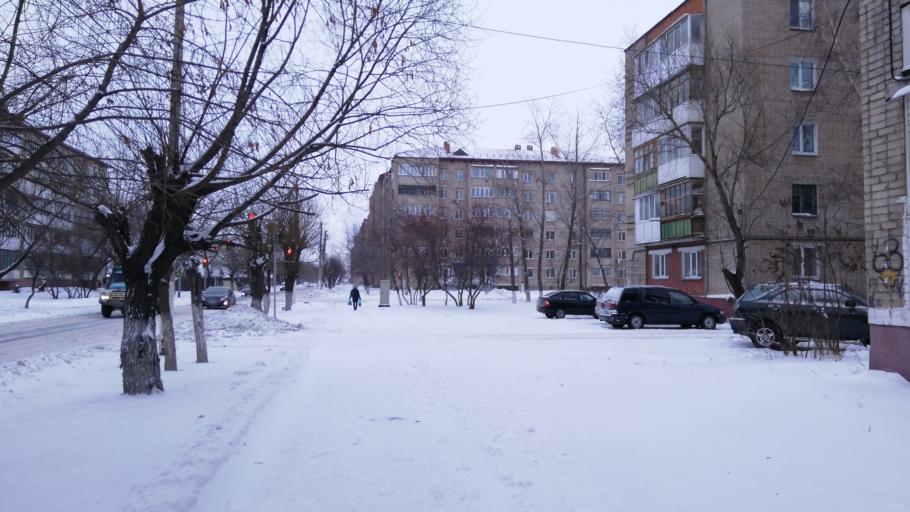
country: KZ
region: Soltustik Qazaqstan
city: Petropavlovsk
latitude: 54.8608
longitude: 69.1702
